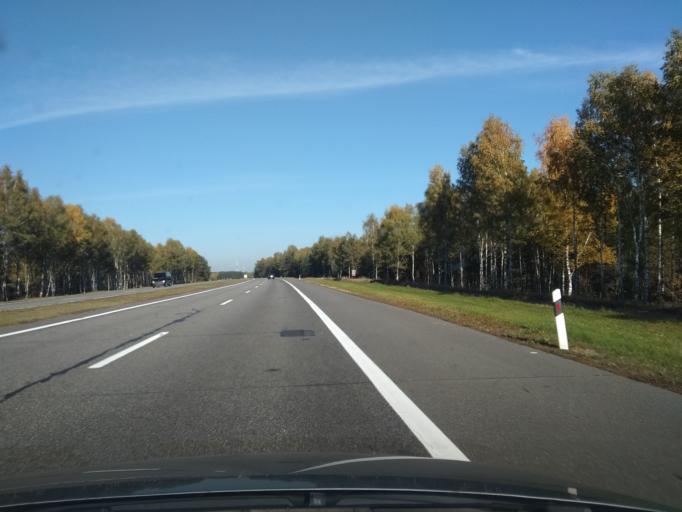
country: BY
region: Brest
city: Baranovichi
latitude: 53.0700
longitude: 25.8797
